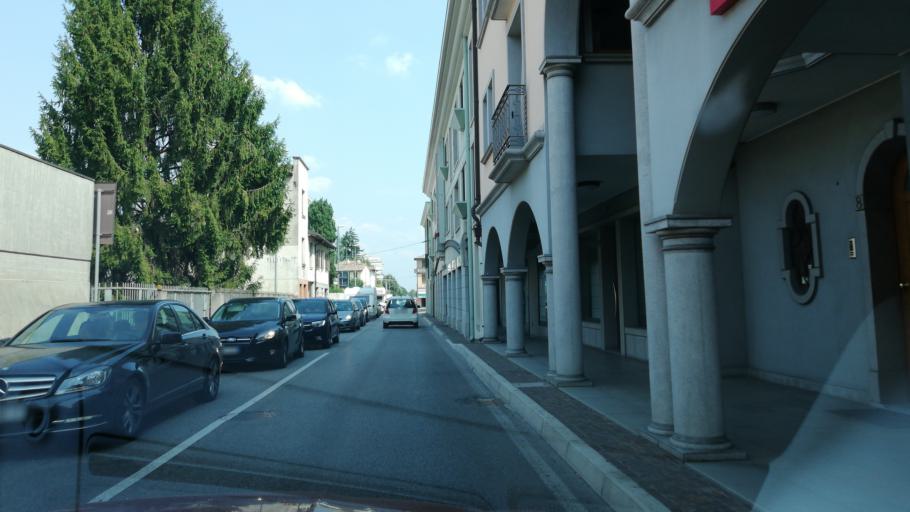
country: IT
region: Friuli Venezia Giulia
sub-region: Provincia di Udine
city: Latisana
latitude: 45.7786
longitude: 12.9964
